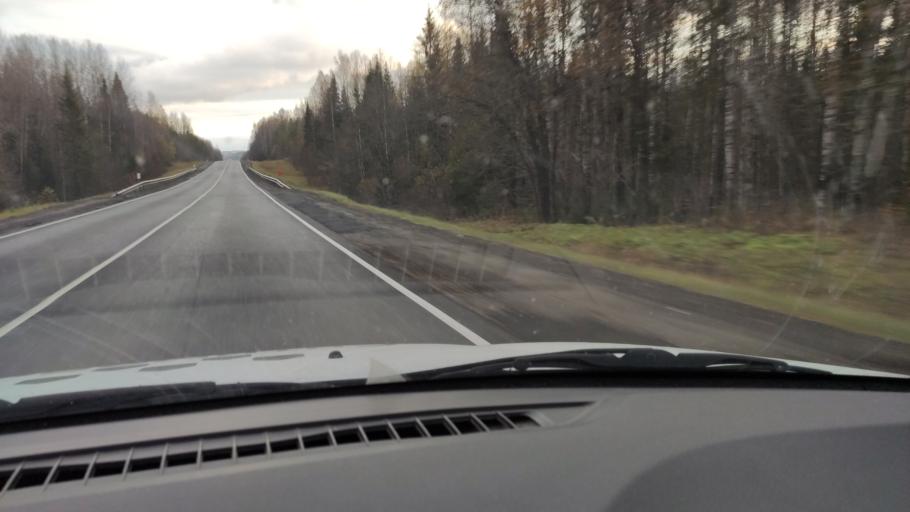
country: RU
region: Kirov
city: Omutninsk
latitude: 58.7442
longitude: 52.0643
